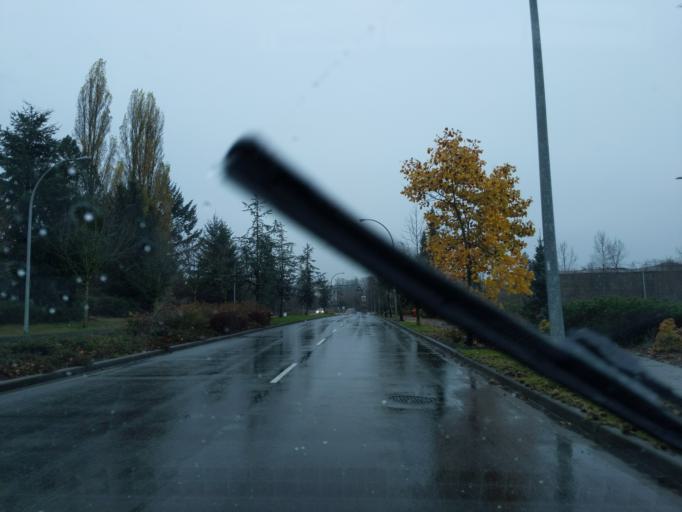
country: CA
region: British Columbia
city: Walnut Grove
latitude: 49.1680
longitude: -122.6627
